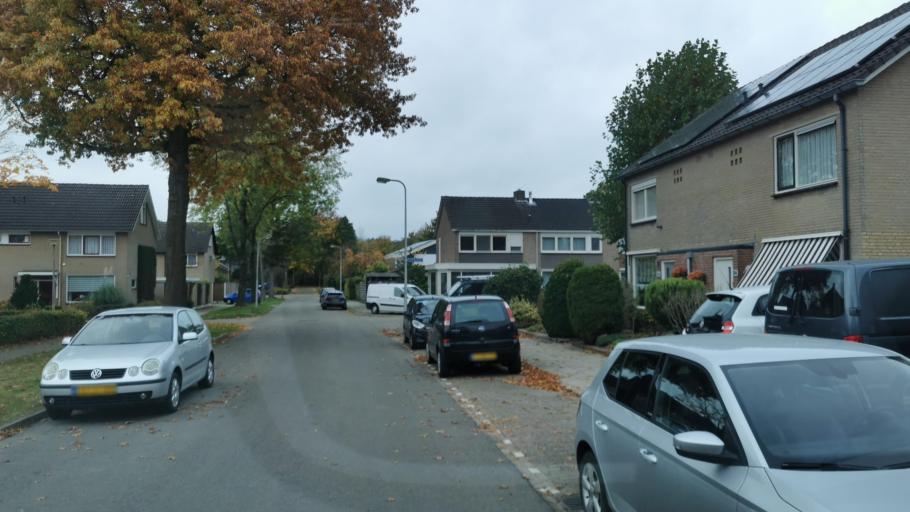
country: NL
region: Overijssel
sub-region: Gemeente Losser
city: Losser
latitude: 52.2524
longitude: 7.0070
